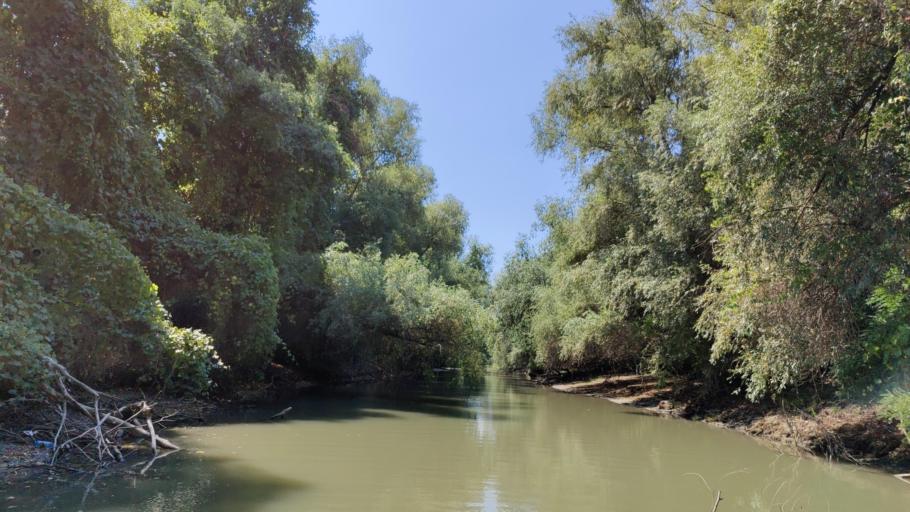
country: RO
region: Tulcea
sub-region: Comuna Pardina
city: Pardina
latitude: 45.2553
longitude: 28.9837
